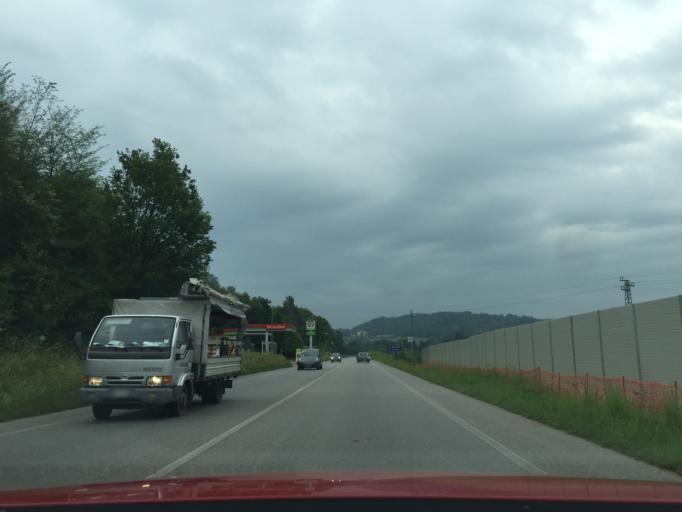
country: IT
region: Tuscany
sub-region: Provincia di Pistoia
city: Serravalle Pistoiese
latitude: 43.9081
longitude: 10.8428
